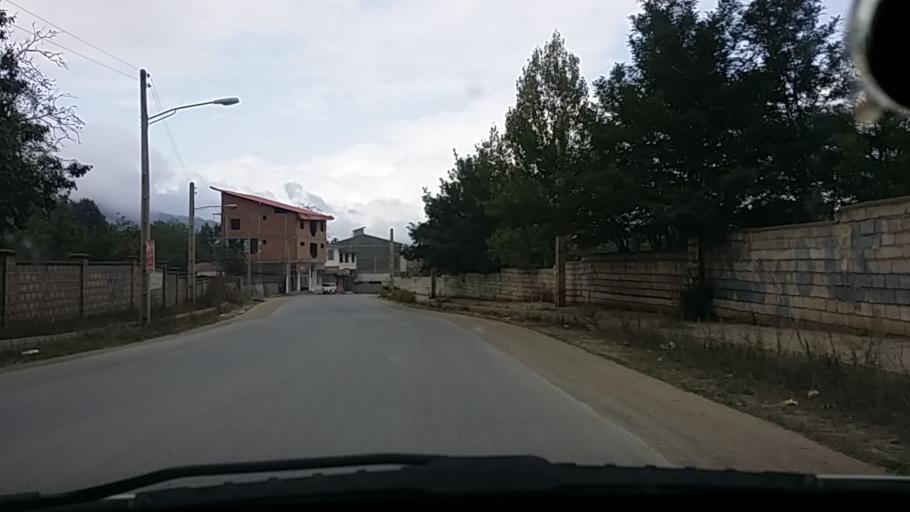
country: IR
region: Mazandaran
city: `Abbasabad
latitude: 36.5044
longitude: 51.1635
